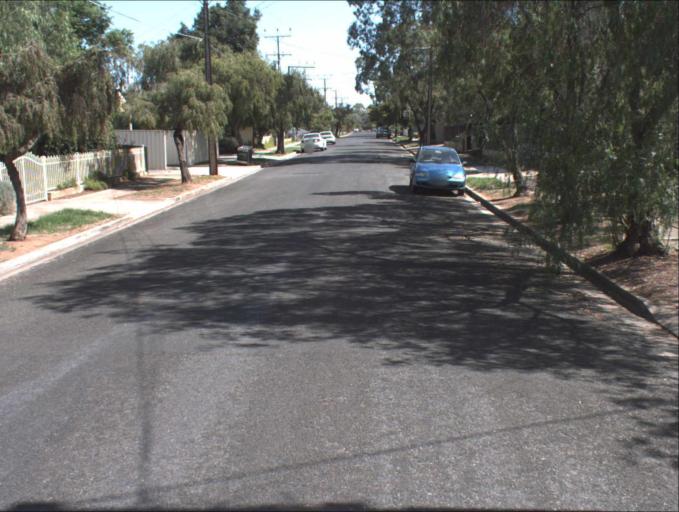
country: AU
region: South Australia
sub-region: Port Adelaide Enfield
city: Klemzig
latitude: -34.8807
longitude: 138.6471
